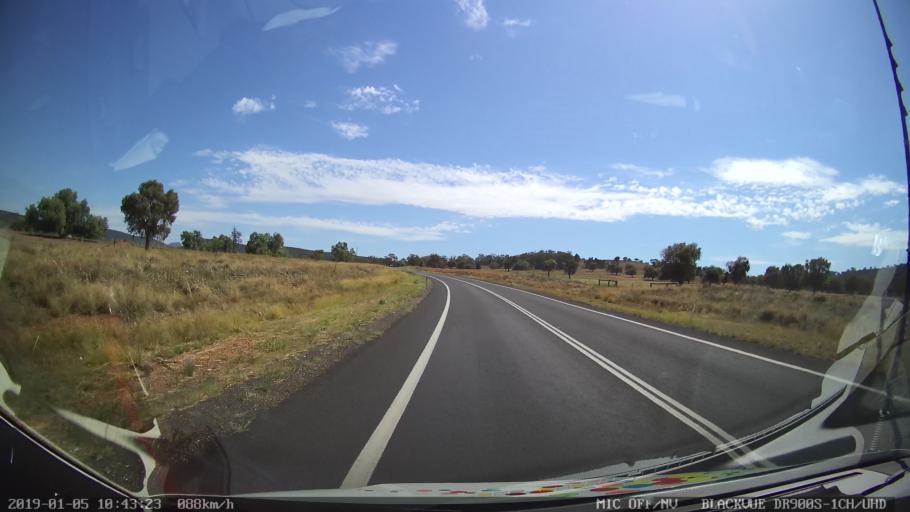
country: AU
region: New South Wales
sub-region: Warrumbungle Shire
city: Coonabarabran
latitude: -31.4654
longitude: 148.9876
